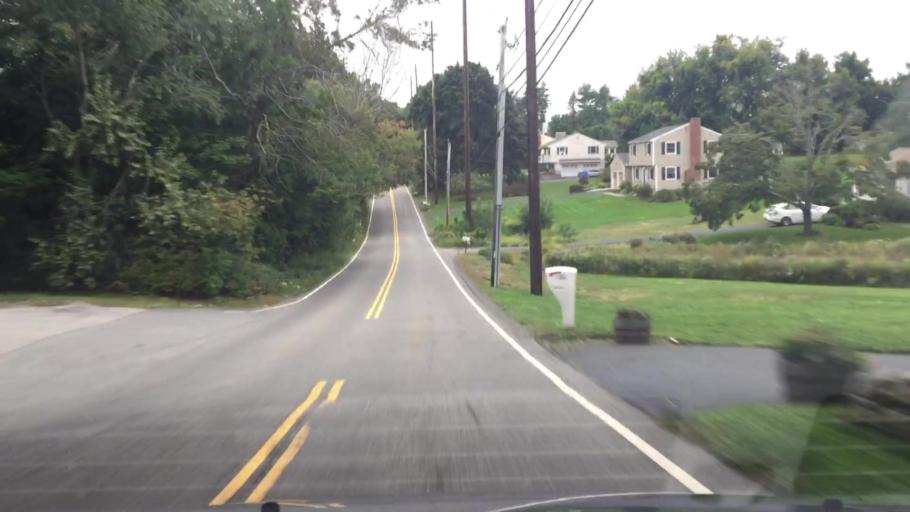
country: US
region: Massachusetts
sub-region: Essex County
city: North Andover
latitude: 42.7301
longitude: -71.1034
